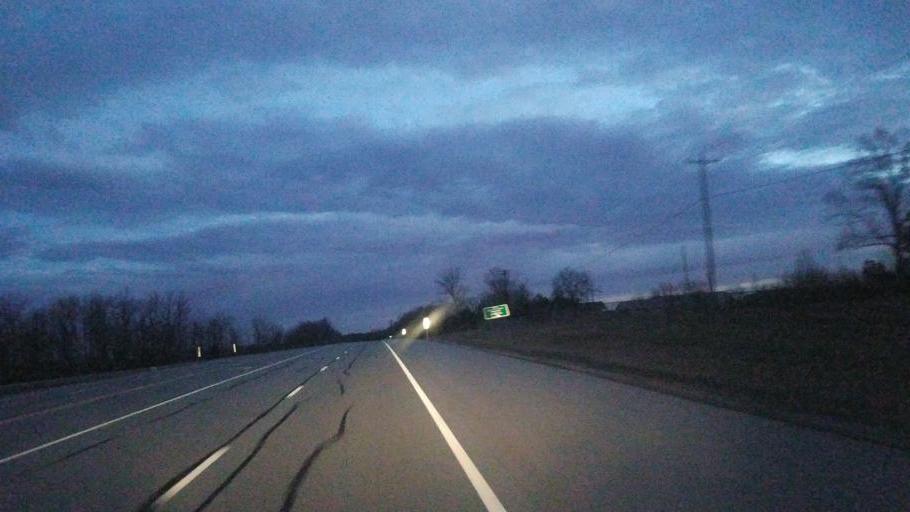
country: US
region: Tennessee
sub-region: Sequatchie County
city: Dunlap
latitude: 35.5309
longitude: -85.4689
